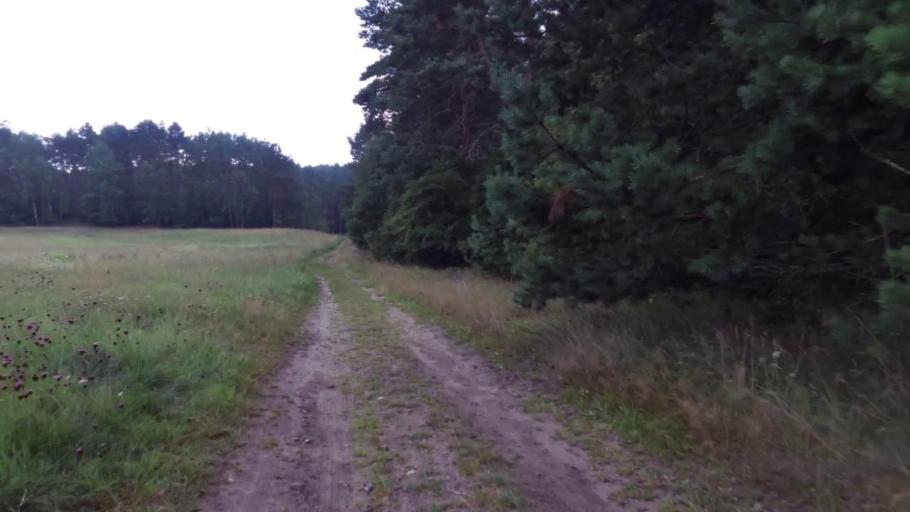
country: PL
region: West Pomeranian Voivodeship
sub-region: Powiat szczecinecki
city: Lubowo
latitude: 53.6026
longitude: 16.3849
